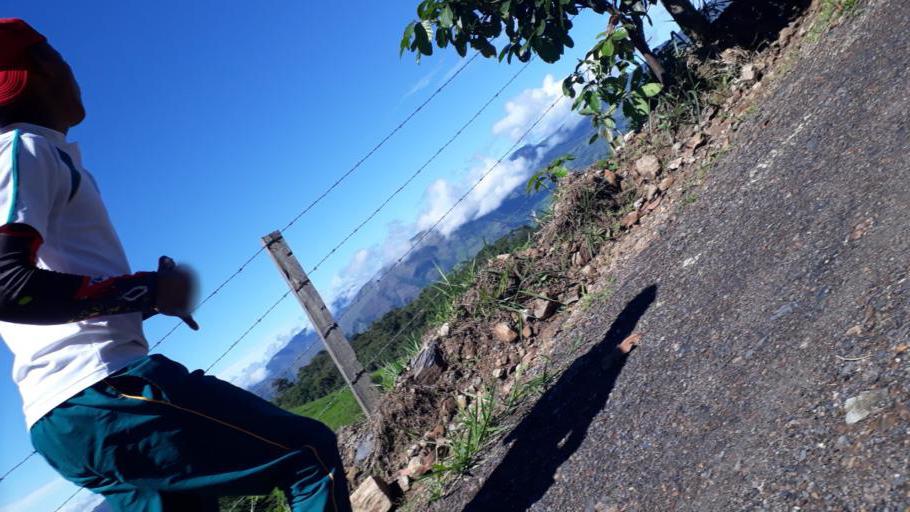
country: CO
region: Casanare
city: Nunchia
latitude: 5.6674
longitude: -72.4275
